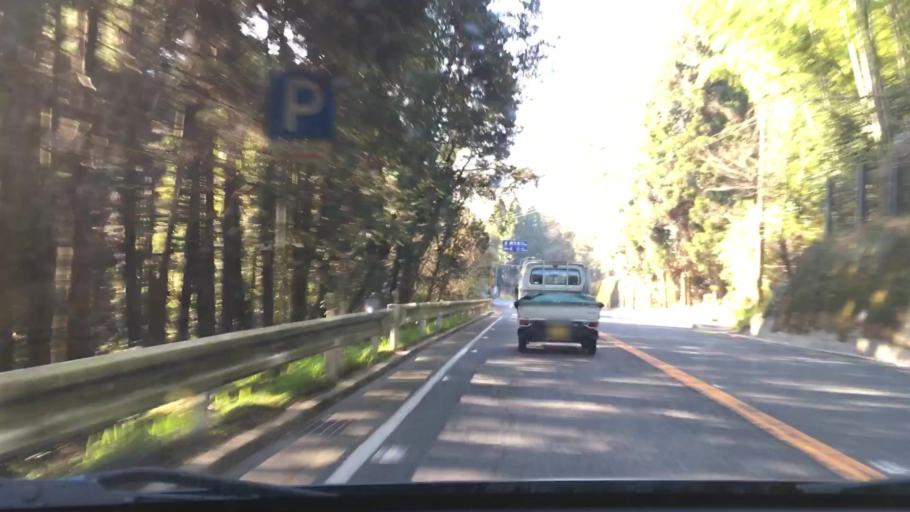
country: JP
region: Kagoshima
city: Sueyoshicho-ninokata
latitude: 31.6642
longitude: 130.9043
